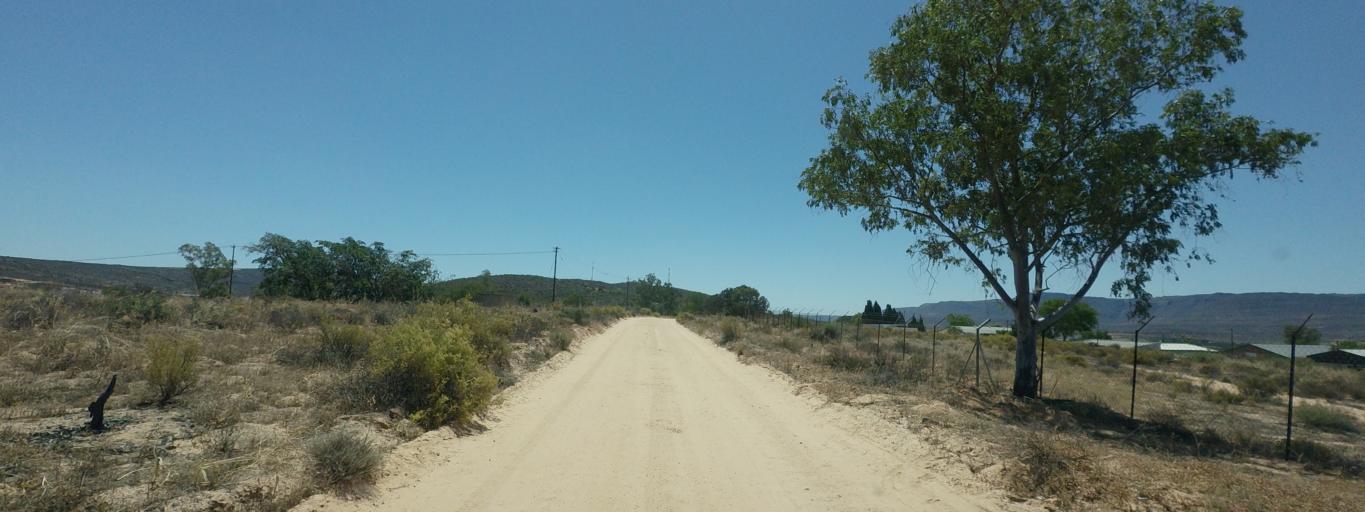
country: ZA
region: Western Cape
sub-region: West Coast District Municipality
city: Clanwilliam
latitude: -32.1887
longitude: 18.8855
